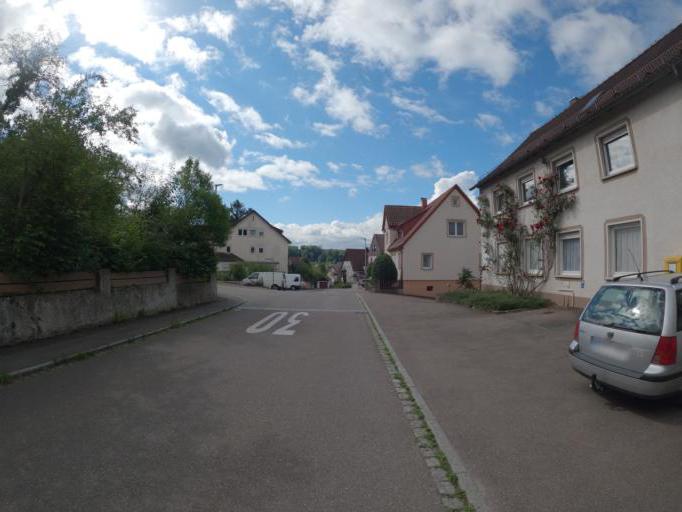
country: DE
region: Baden-Wuerttemberg
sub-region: Regierungsbezirk Stuttgart
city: Ebersbach an der Fils
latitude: 48.7171
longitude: 9.5220
